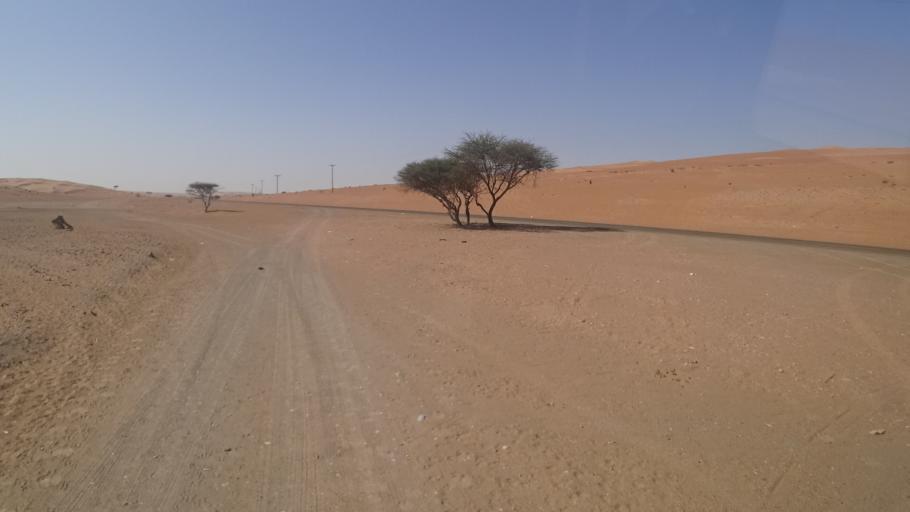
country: OM
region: Ash Sharqiyah
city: Al Qabil
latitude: 22.4804
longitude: 58.7119
